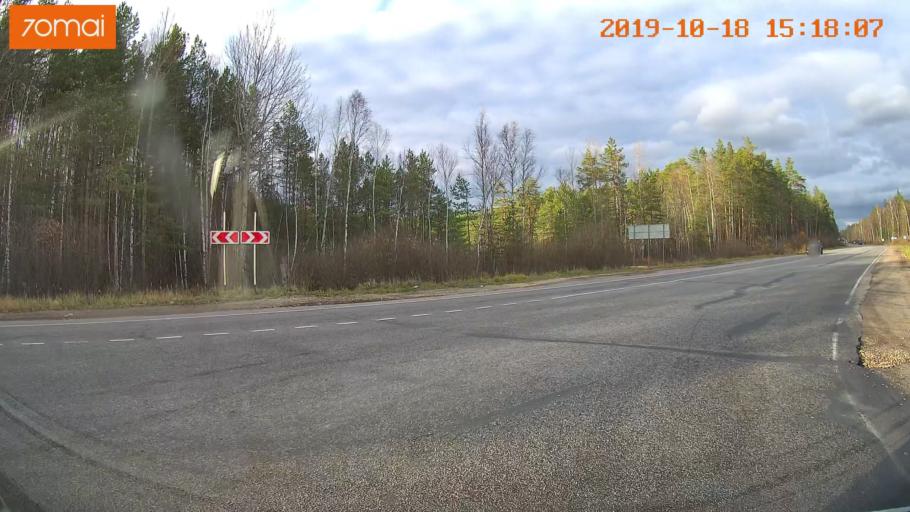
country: RU
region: Vladimir
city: Anopino
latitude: 55.6571
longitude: 40.7268
